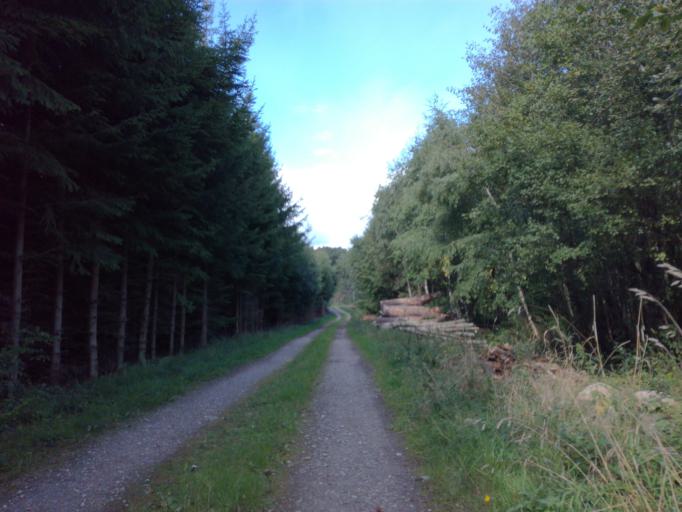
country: DK
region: South Denmark
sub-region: Fredericia Kommune
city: Snoghoj
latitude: 55.5136
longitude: 9.6973
